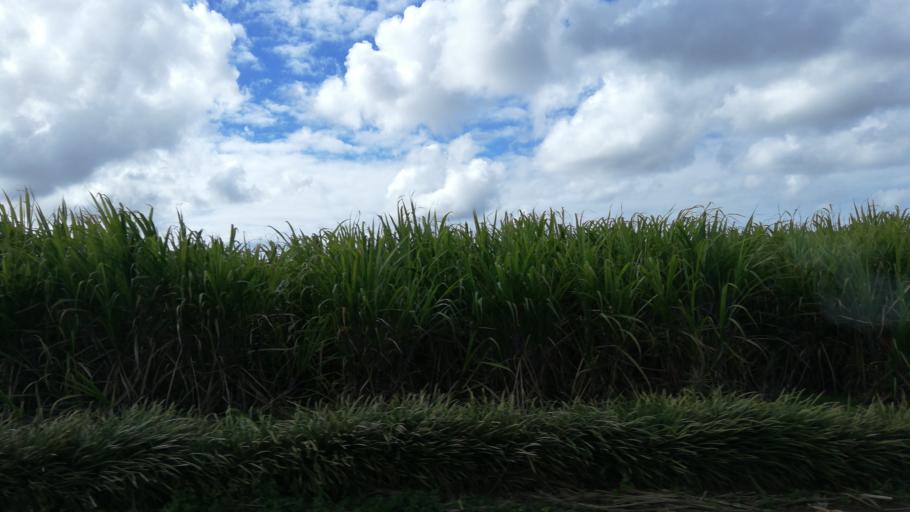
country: MU
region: Flacq
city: Camp de Masque
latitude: -20.2166
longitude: 57.6748
